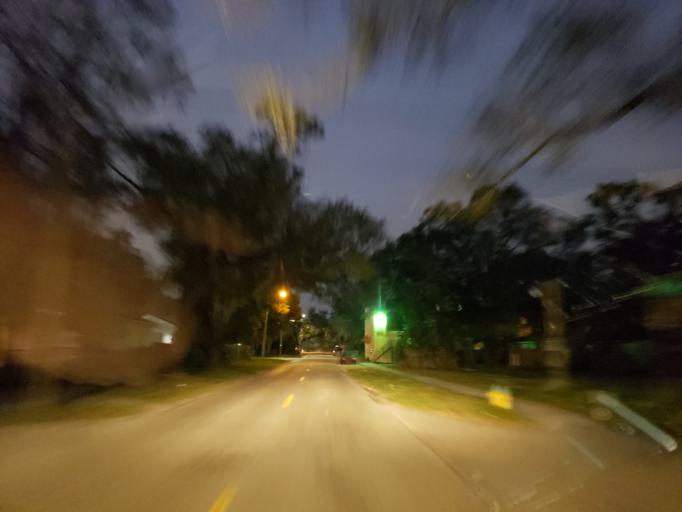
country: US
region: Florida
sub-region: Hillsborough County
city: University
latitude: 28.0226
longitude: -82.4477
